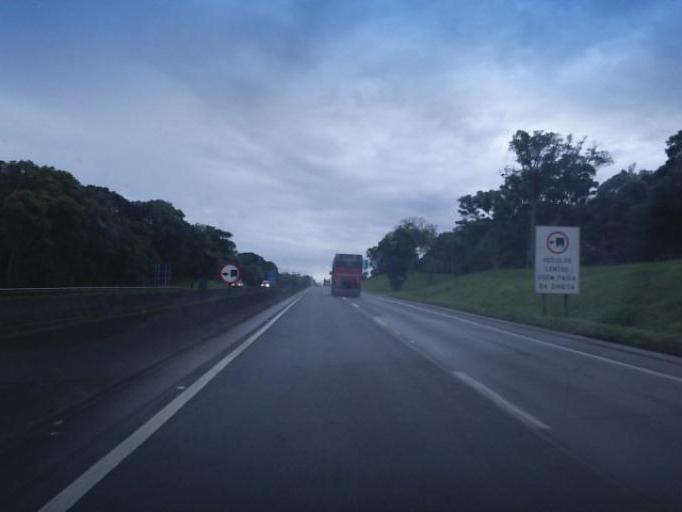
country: BR
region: Parana
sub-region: Sao Jose Dos Pinhais
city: Sao Jose dos Pinhais
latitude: -25.7540
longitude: -49.1265
